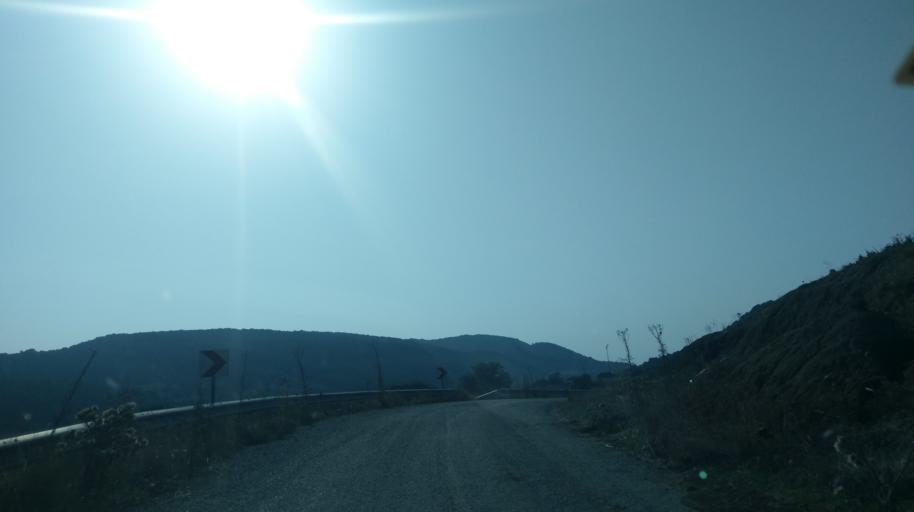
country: CY
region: Ammochostos
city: Rizokarpaso
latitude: 35.5560
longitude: 34.3712
